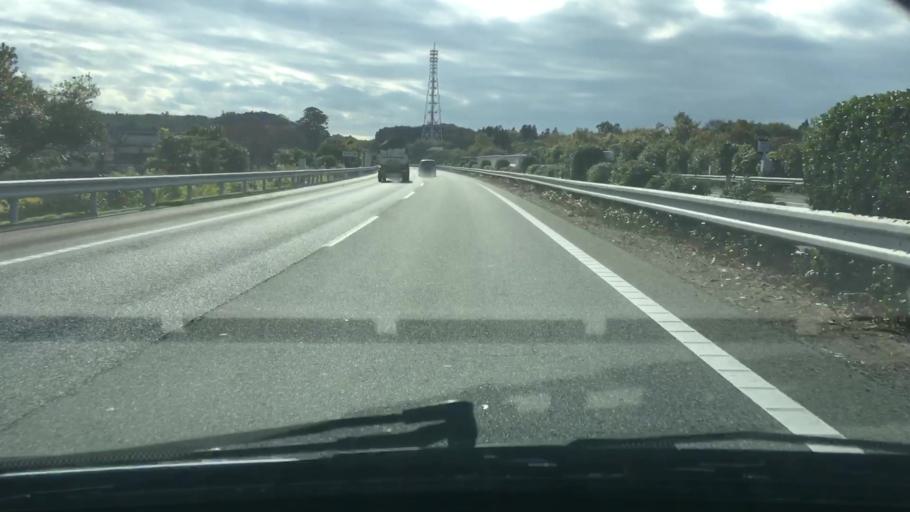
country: JP
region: Chiba
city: Ichihara
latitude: 35.4768
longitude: 140.0816
